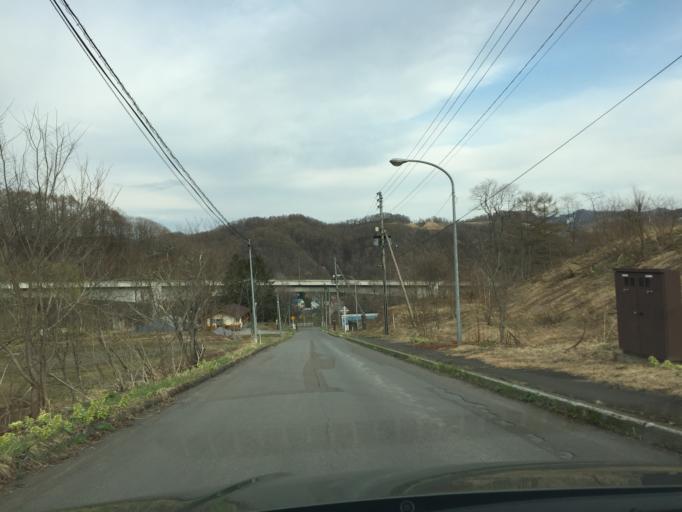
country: JP
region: Hokkaido
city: Utashinai
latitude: 43.5208
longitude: 142.0215
